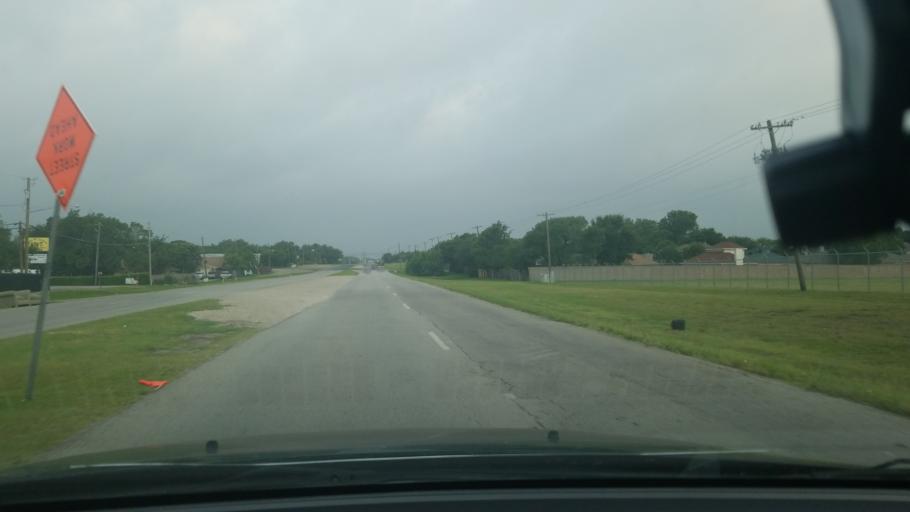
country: US
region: Texas
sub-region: Dallas County
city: Balch Springs
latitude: 32.7684
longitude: -96.6577
